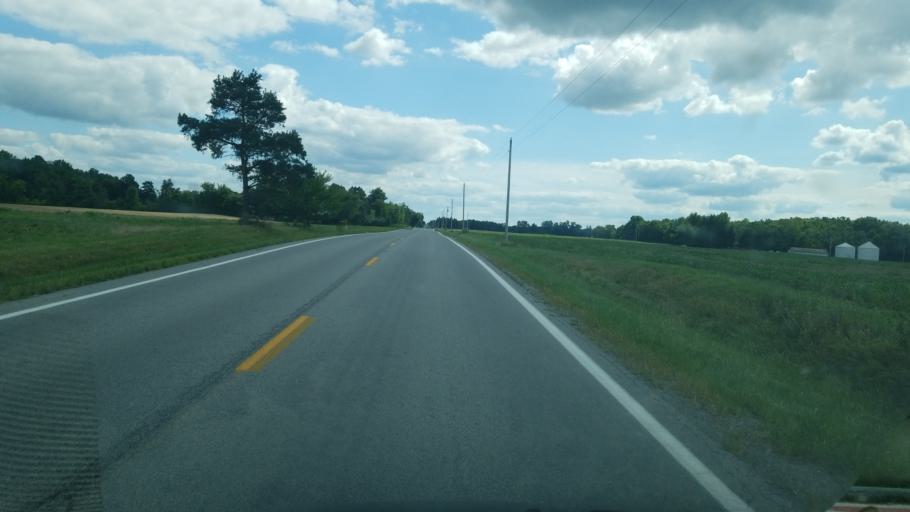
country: US
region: Ohio
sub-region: Allen County
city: Lima
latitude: 40.6767
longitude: -83.9758
